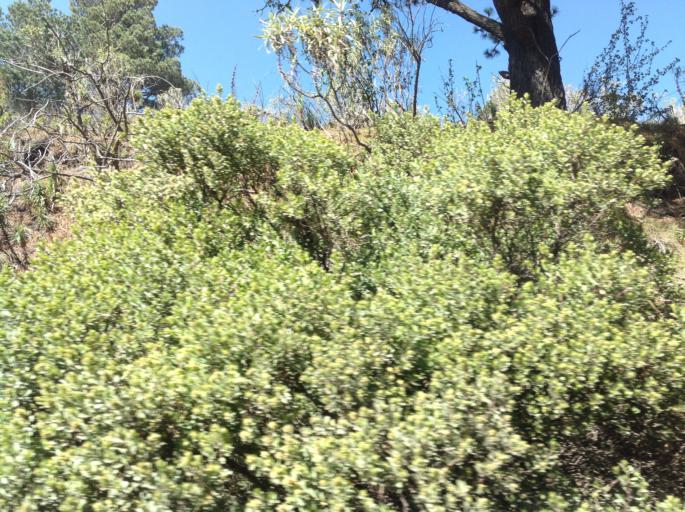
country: MX
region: Mexico
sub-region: Amecameca
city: San Diego Huehuecalco
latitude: 19.0936
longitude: -98.6524
